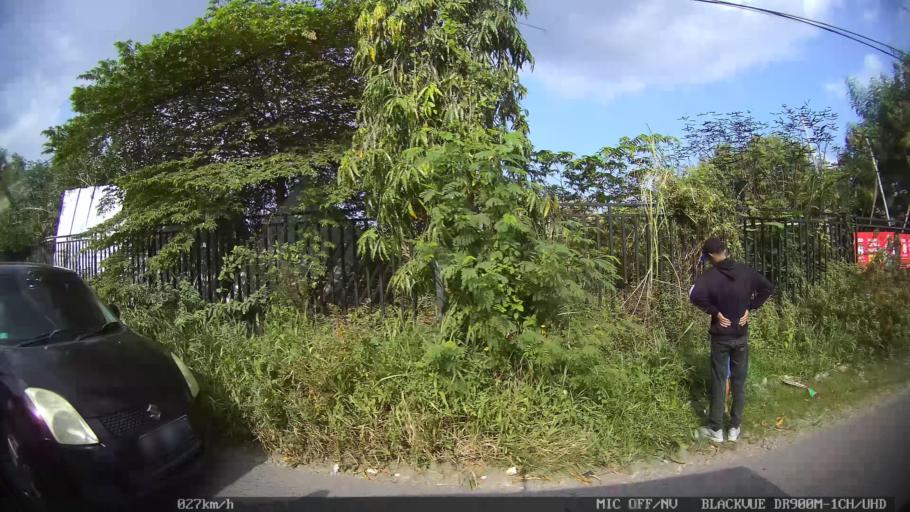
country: ID
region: Daerah Istimewa Yogyakarta
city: Yogyakarta
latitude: -7.7872
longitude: 110.3488
